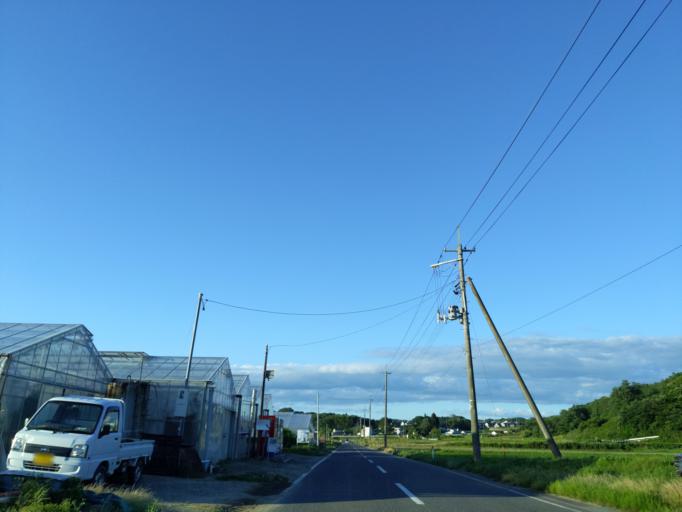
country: JP
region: Fukushima
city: Koriyama
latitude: 37.4145
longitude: 140.4146
